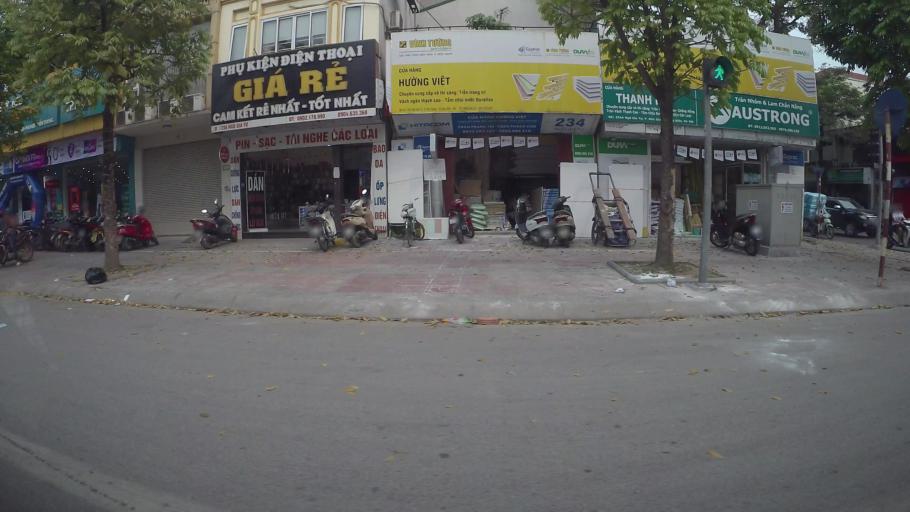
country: VN
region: Ha Noi
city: Hoan Kiem
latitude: 21.0627
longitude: 105.8956
